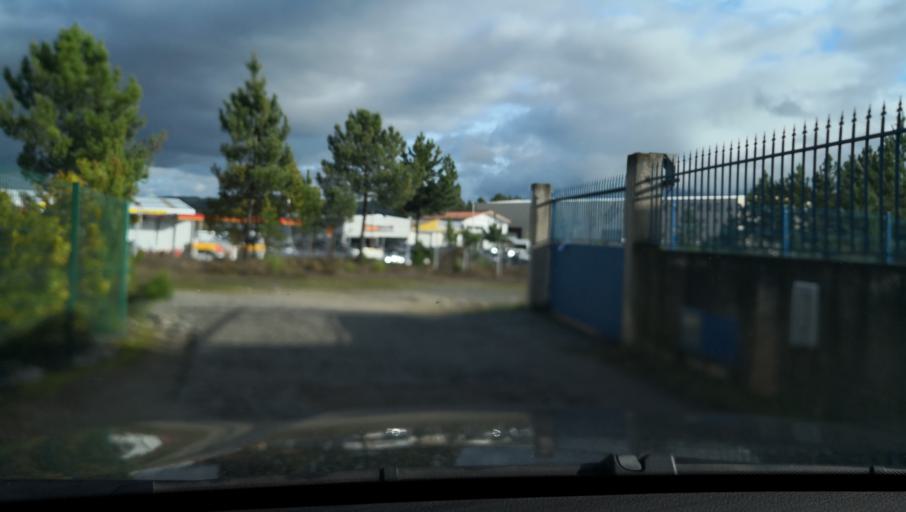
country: PT
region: Vila Real
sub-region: Vila Real
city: Vila Real
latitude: 41.2749
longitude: -7.7156
